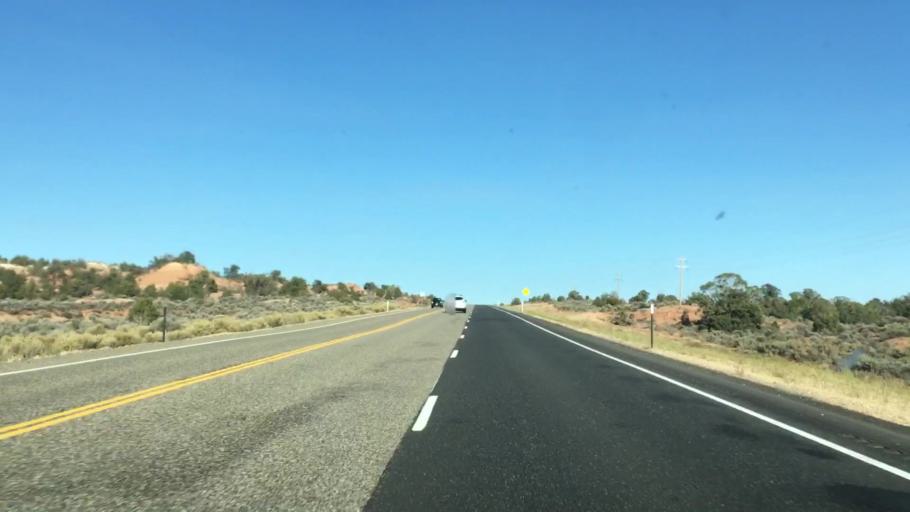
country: US
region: Utah
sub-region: Kane County
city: Kanab
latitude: 37.0584
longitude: -112.1928
